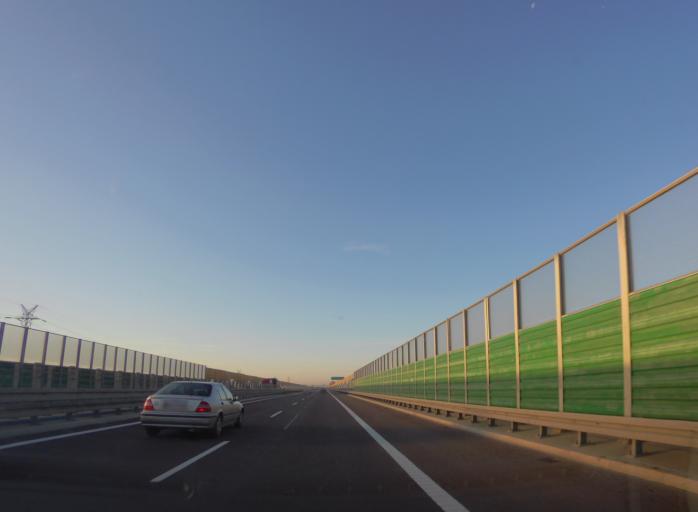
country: PL
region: Subcarpathian Voivodeship
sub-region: Powiat rzeszowski
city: Trzebownisko
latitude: 50.1075
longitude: 22.0695
